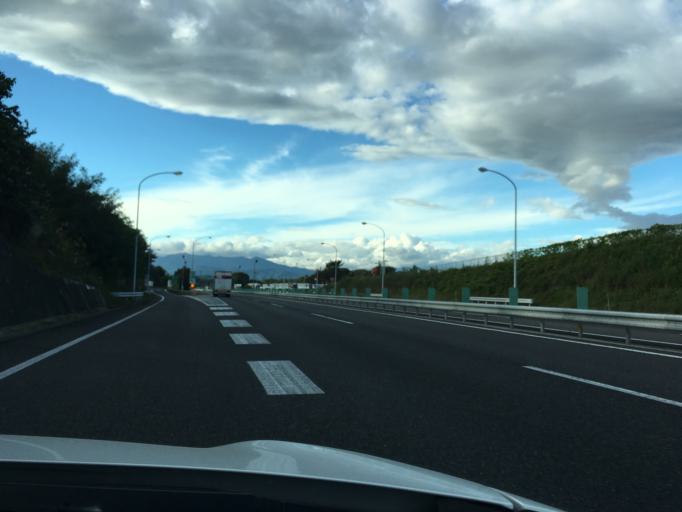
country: JP
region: Fukushima
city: Koriyama
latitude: 37.3513
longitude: 140.3253
